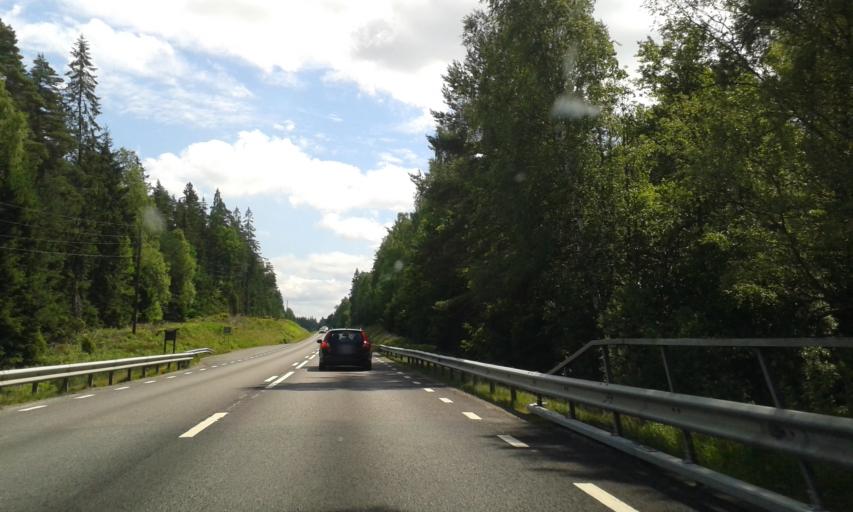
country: SE
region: Joenkoeping
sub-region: Varnamo Kommun
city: Bor
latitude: 57.0581
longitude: 14.2019
